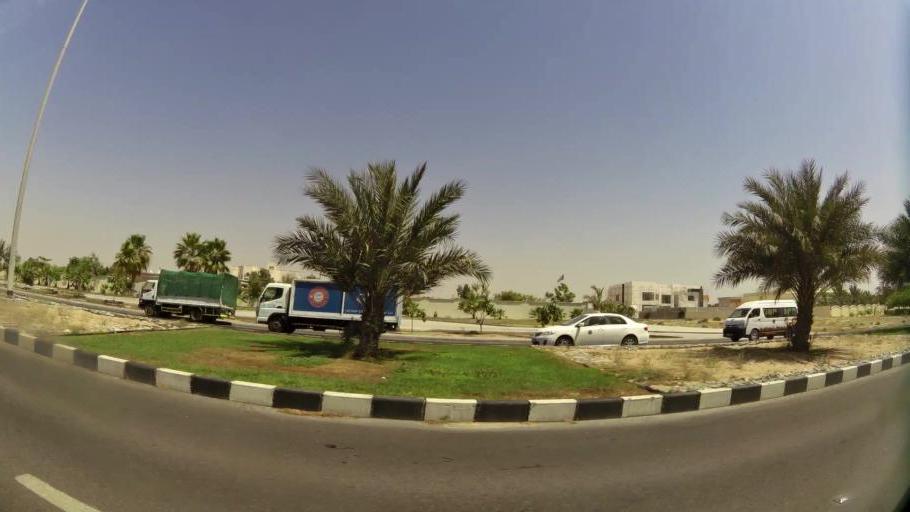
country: AE
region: Ajman
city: Ajman
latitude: 25.4236
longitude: 55.4951
